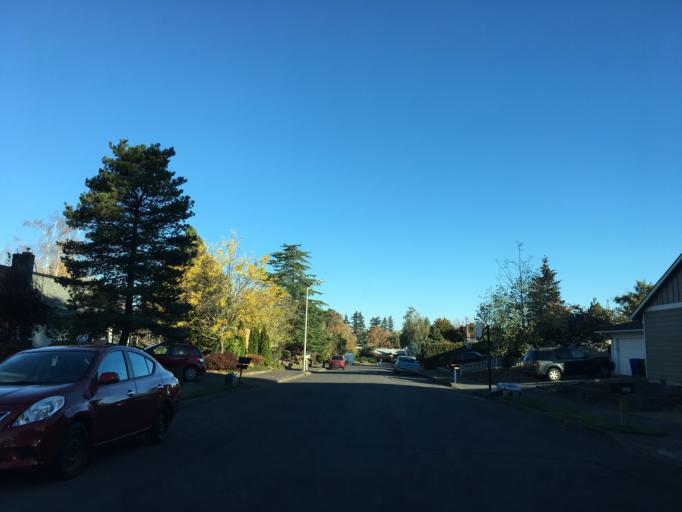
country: US
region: Oregon
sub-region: Multnomah County
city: Gresham
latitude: 45.5079
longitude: -122.4062
